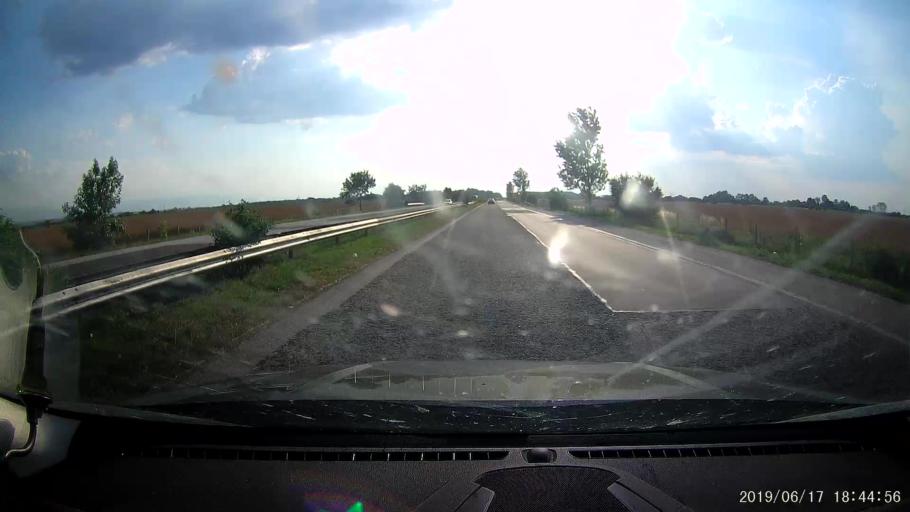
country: BG
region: Stara Zagora
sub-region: Obshtina Chirpan
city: Chirpan
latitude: 42.1936
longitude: 25.1660
